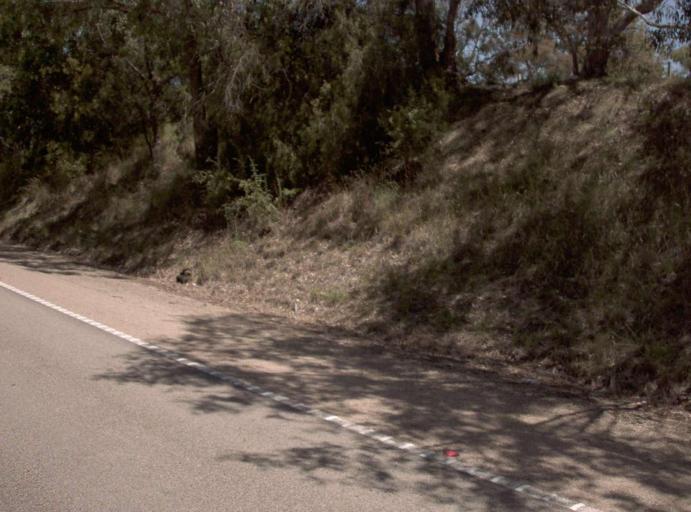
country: AU
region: Victoria
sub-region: East Gippsland
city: Bairnsdale
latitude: -37.7182
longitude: 147.8053
